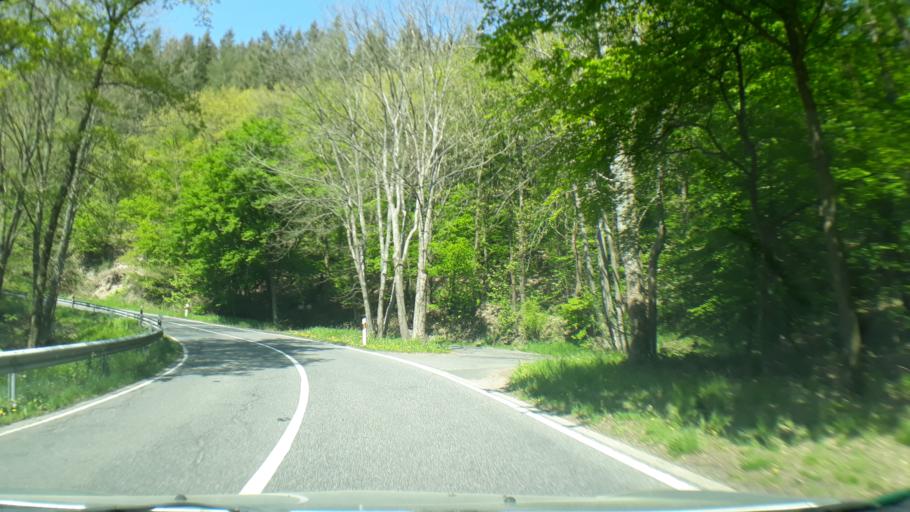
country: DE
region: North Rhine-Westphalia
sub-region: Regierungsbezirk Koln
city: Nideggen
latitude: 50.6826
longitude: 6.4346
